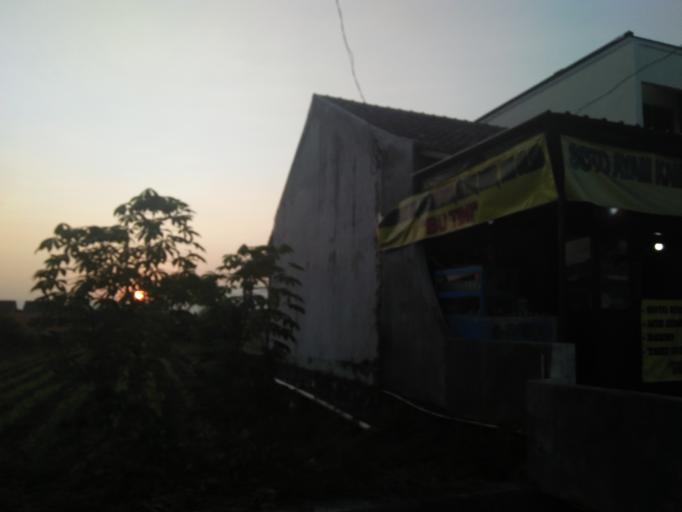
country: ID
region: Daerah Istimewa Yogyakarta
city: Sewon
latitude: -7.8528
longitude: 110.4099
